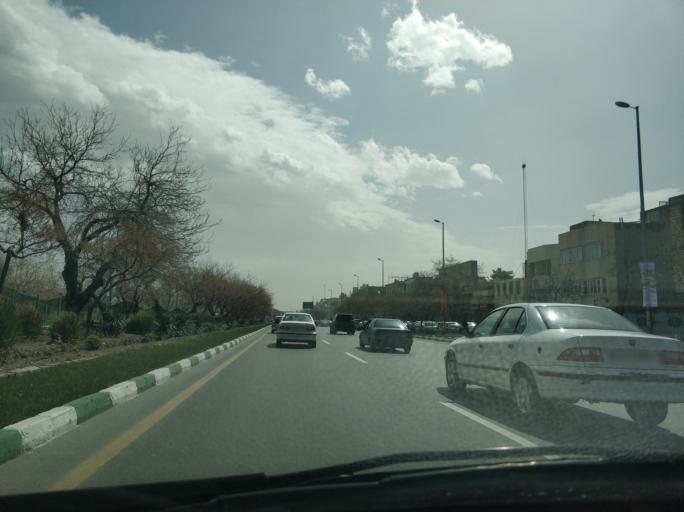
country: IR
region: Razavi Khorasan
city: Mashhad
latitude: 36.3256
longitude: 59.5065
